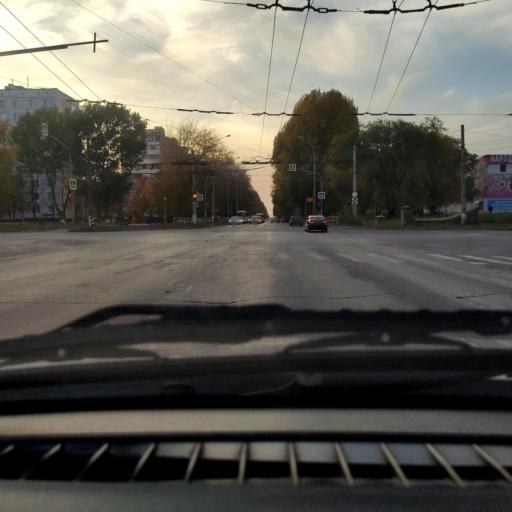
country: RU
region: Samara
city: Tol'yatti
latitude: 53.5380
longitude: 49.2790
